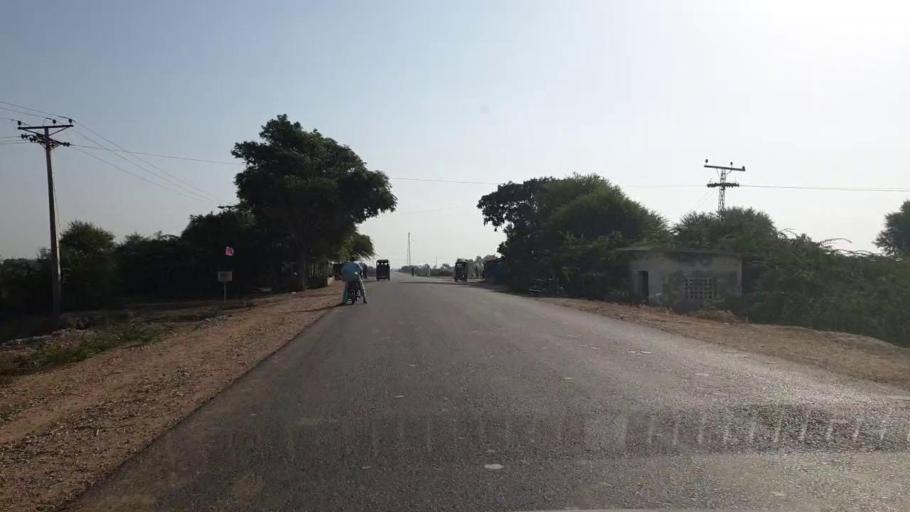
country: PK
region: Sindh
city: Badin
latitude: 24.6586
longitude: 68.9437
